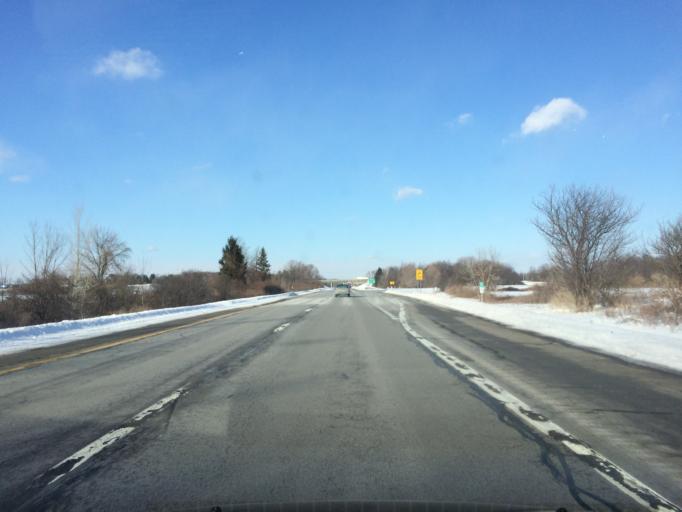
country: US
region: New York
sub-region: Genesee County
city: Bergen
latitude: 43.0696
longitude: -77.9359
